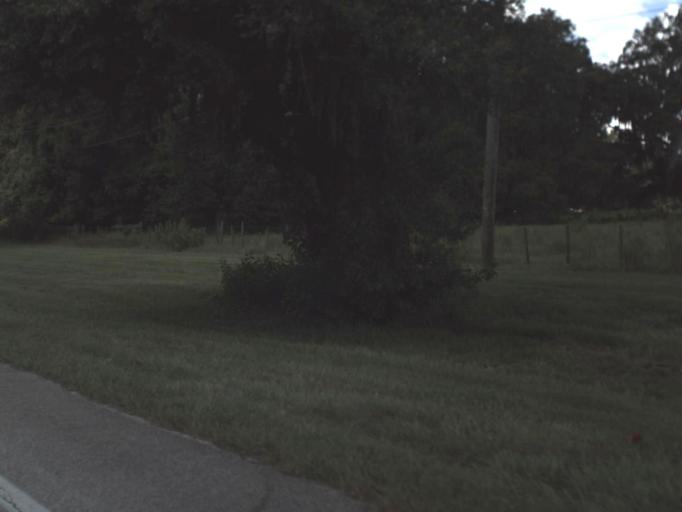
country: US
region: Florida
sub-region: Polk County
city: Polk City
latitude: 28.1595
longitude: -81.8596
